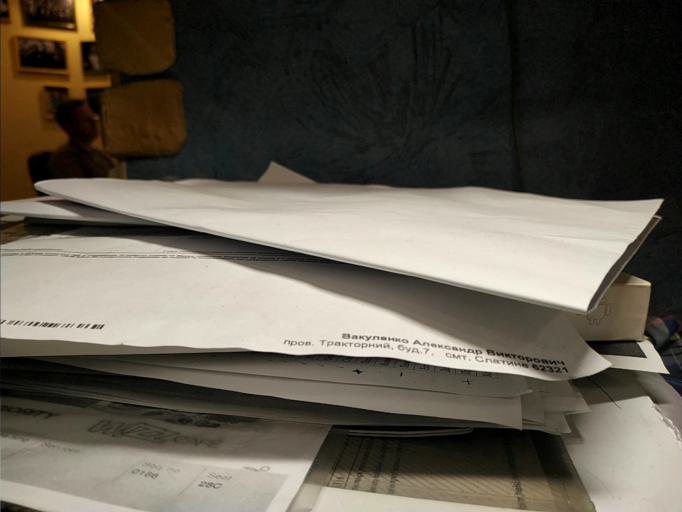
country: RU
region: Tverskaya
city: Zubtsov
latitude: 56.1280
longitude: 34.5287
